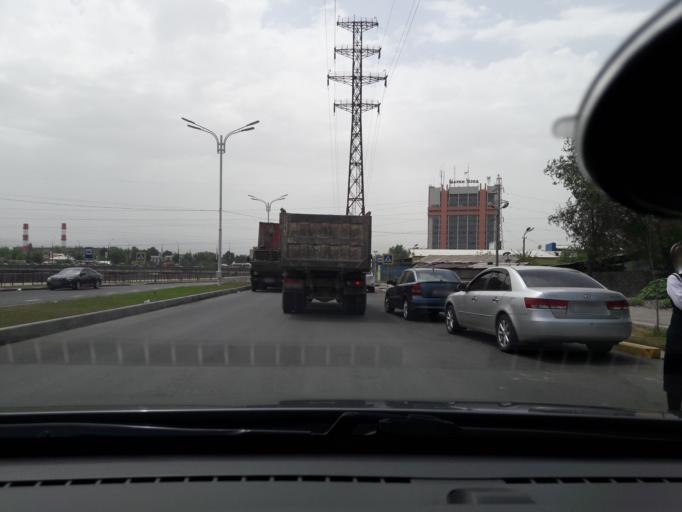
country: TJ
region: Dushanbe
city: Dushanbe
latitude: 38.5622
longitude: 68.7695
